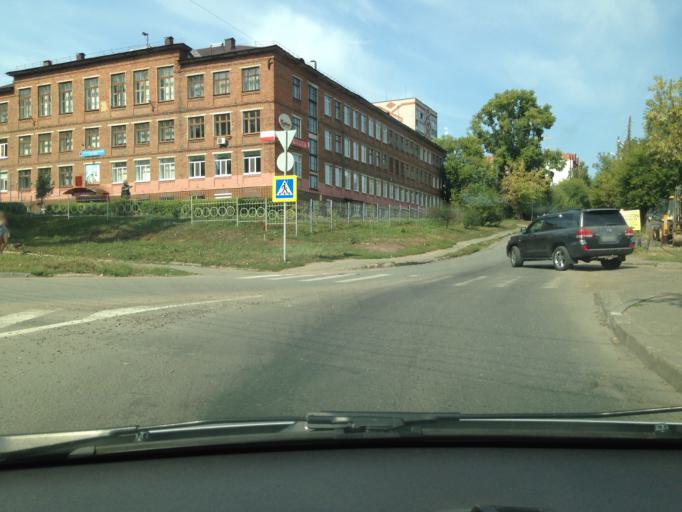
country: RU
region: Udmurtiya
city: Izhevsk
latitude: 56.8614
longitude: 53.1883
